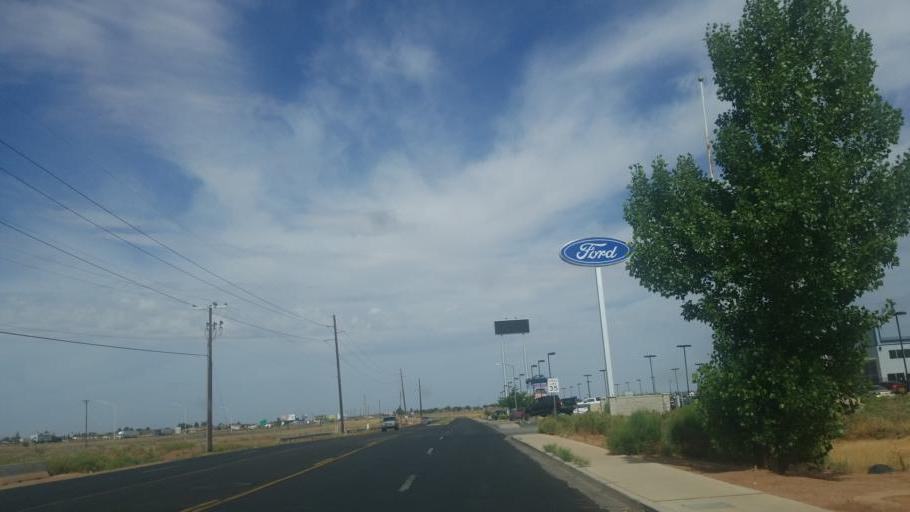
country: US
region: Arizona
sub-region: Navajo County
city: Winslow
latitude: 35.0409
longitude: -110.7025
